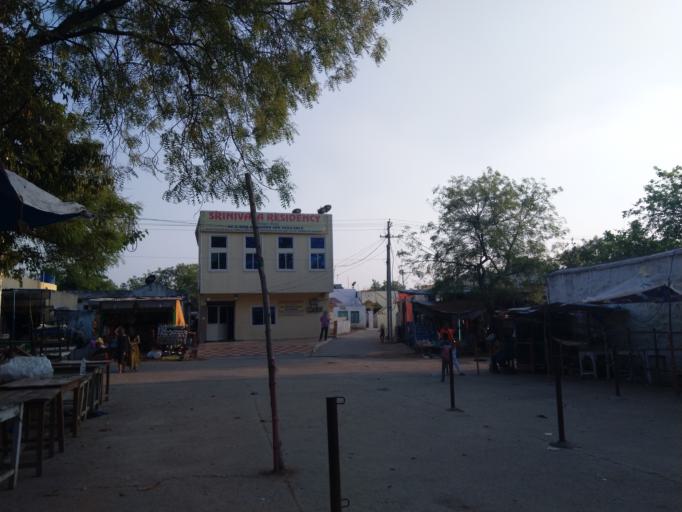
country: IN
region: Telangana
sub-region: Rangareddi
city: Sriramnagar
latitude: 17.3582
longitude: 78.2991
